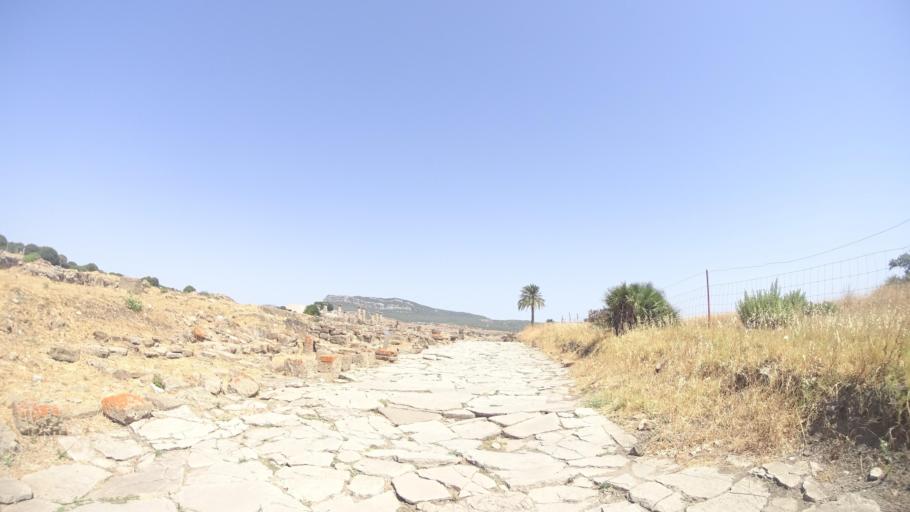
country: ES
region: Andalusia
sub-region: Provincia de Cadiz
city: Zahara de los Atunes
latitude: 36.0894
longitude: -5.7756
